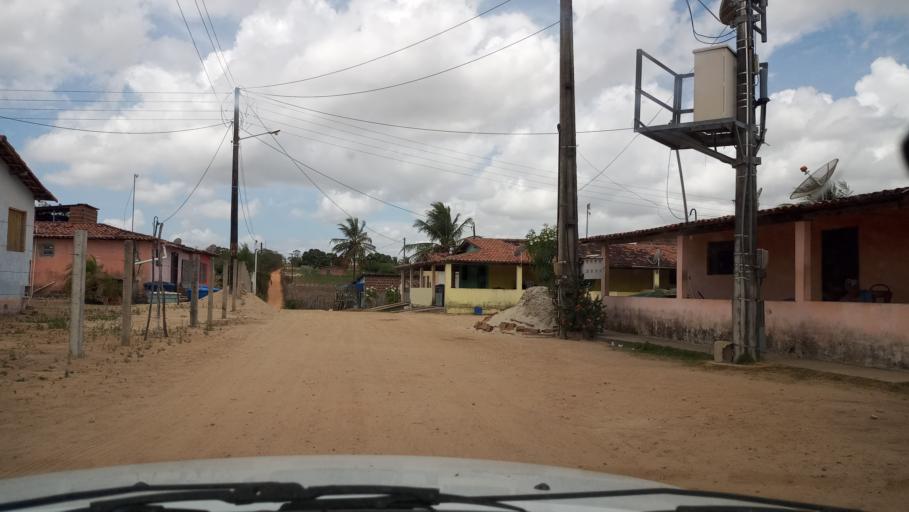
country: BR
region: Rio Grande do Norte
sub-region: Goianinha
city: Goianinha
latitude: -6.3014
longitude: -35.2749
